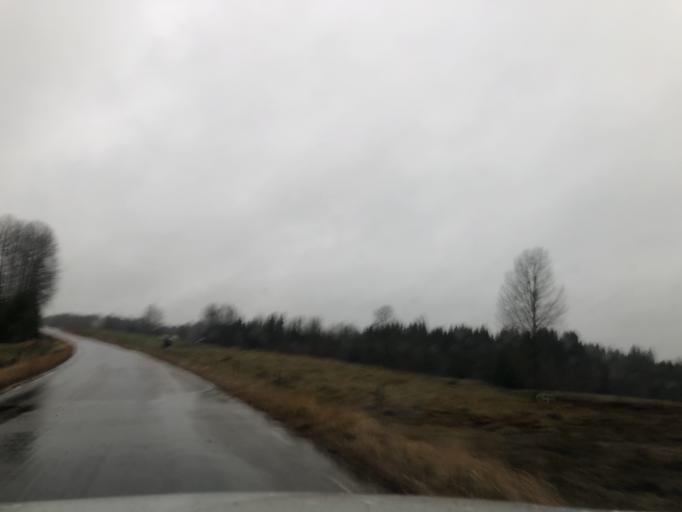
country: SE
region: Vaestra Goetaland
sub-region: Ulricehamns Kommun
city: Ulricehamn
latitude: 57.8568
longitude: 13.5493
